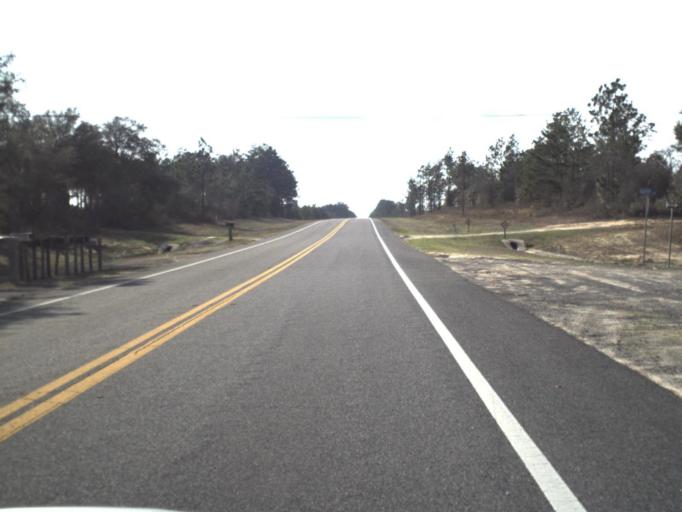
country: US
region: Florida
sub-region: Bay County
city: Youngstown
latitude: 30.4362
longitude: -85.4708
